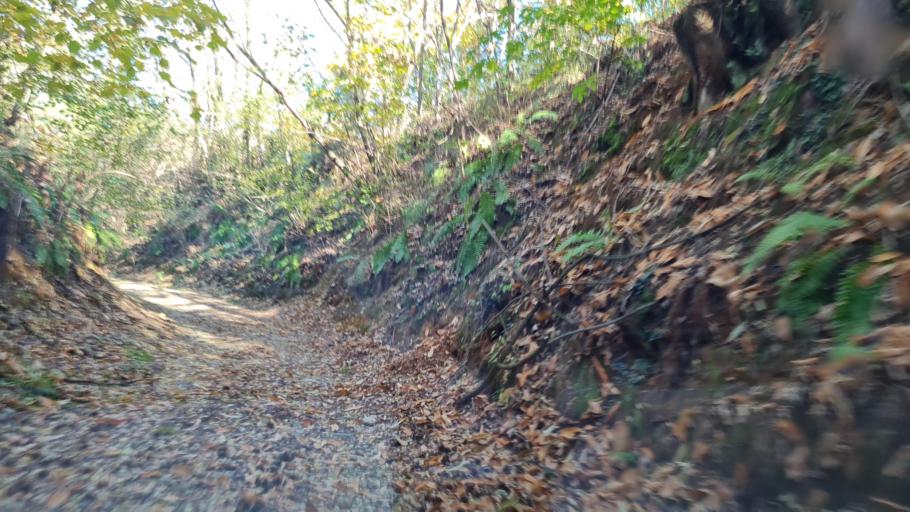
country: IT
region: Piedmont
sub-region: Provincia di Biella
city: Masserano
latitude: 45.5763
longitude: 8.2316
